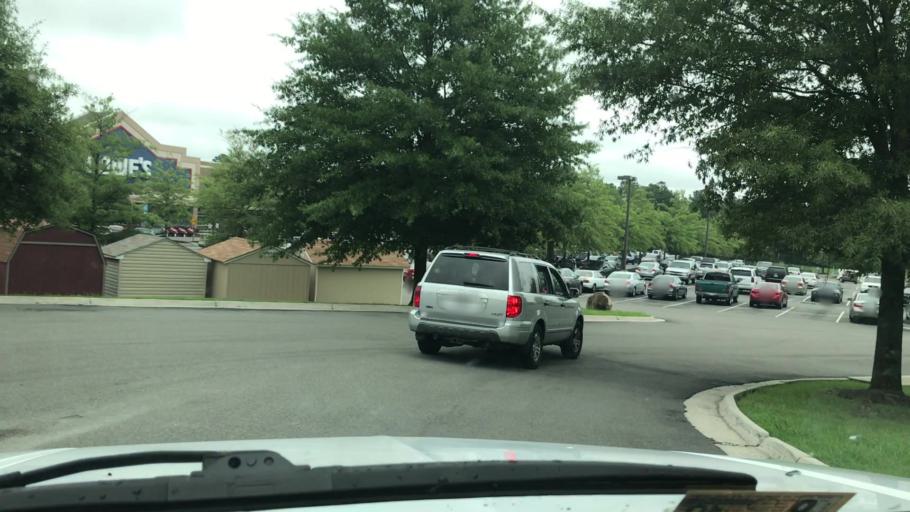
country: US
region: Virginia
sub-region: Henrico County
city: Short Pump
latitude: 37.6550
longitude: -77.6109
